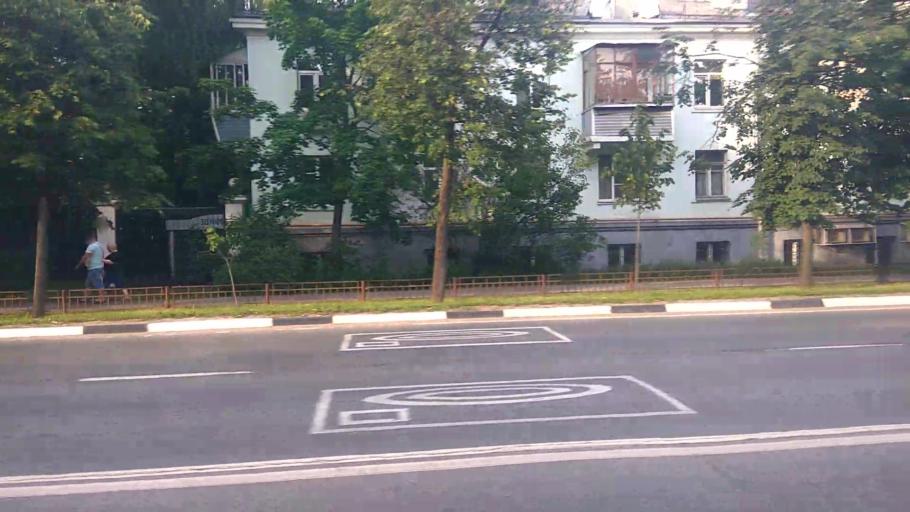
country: RU
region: Moskovskaya
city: Mytishchi
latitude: 55.9132
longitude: 37.7314
